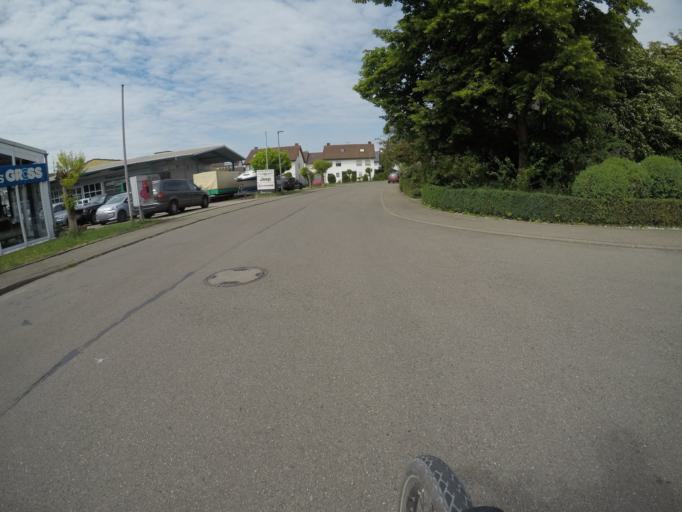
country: DE
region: Baden-Wuerttemberg
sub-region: Regierungsbezirk Stuttgart
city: Notzingen
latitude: 48.6709
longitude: 9.4552
